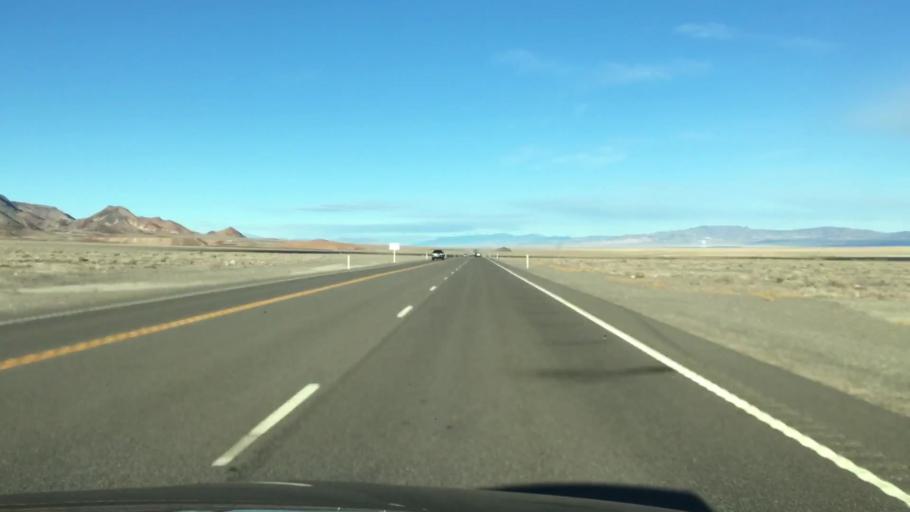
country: US
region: Nevada
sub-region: Nye County
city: Tonopah
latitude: 38.0524
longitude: -117.6540
